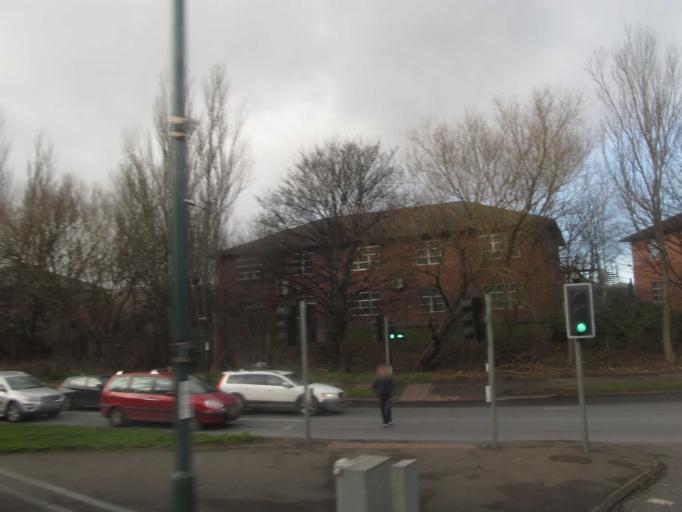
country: GB
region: England
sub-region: Nottinghamshire
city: Hucknall
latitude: 52.9867
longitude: -1.2040
